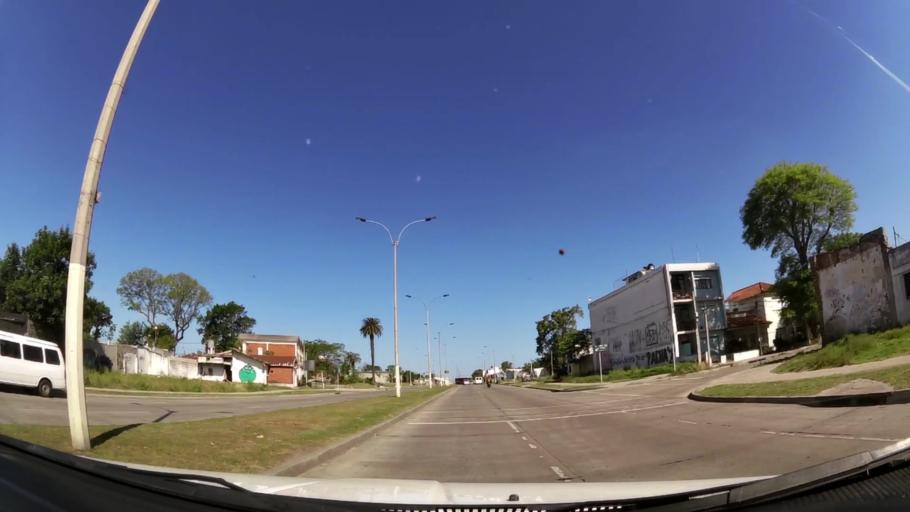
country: UY
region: Canelones
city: La Paz
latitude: -34.8302
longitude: -56.2157
